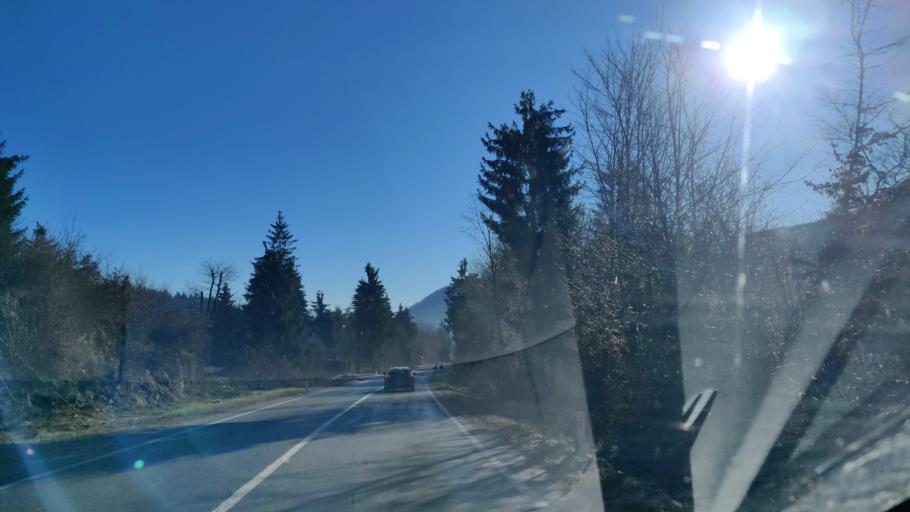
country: SI
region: Logatec
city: Logatec
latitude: 45.8800
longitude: 14.2070
